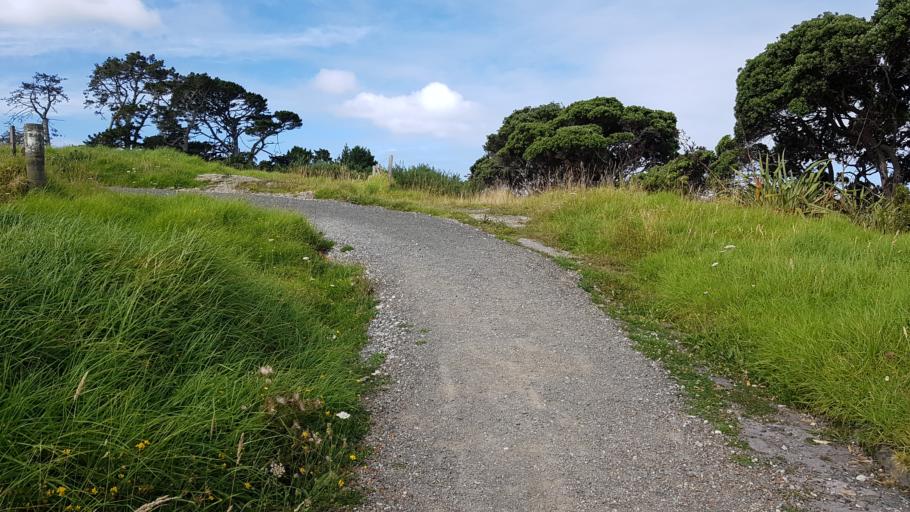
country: NZ
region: Auckland
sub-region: Auckland
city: Rothesay Bay
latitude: -36.6670
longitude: 174.7460
